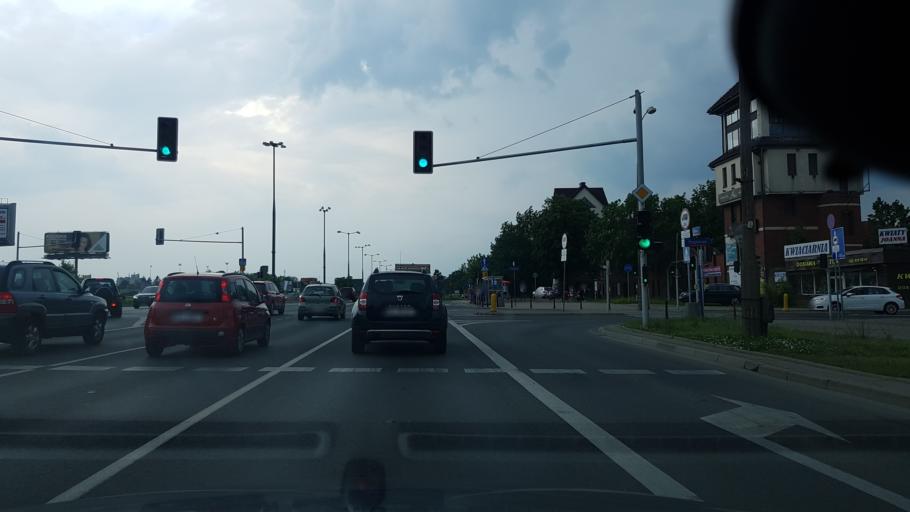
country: PL
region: Masovian Voivodeship
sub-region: Warszawa
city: Bialoleka
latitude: 52.3434
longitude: 20.9520
